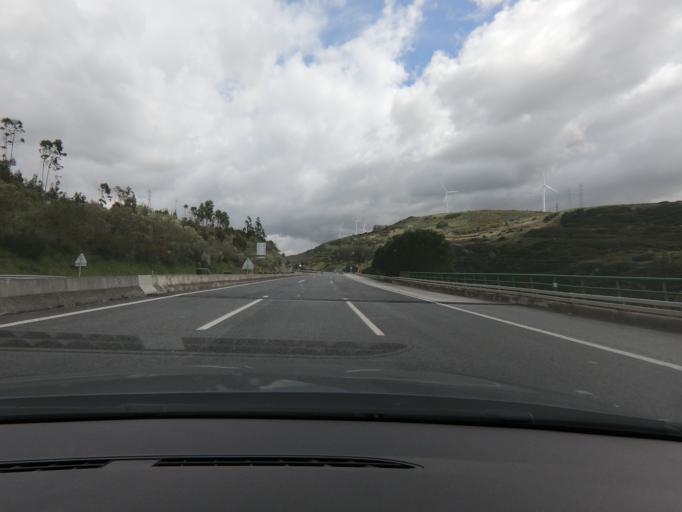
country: PT
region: Lisbon
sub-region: Loures
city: Santo Antao do Tojal
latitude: 38.8765
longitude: -9.1329
